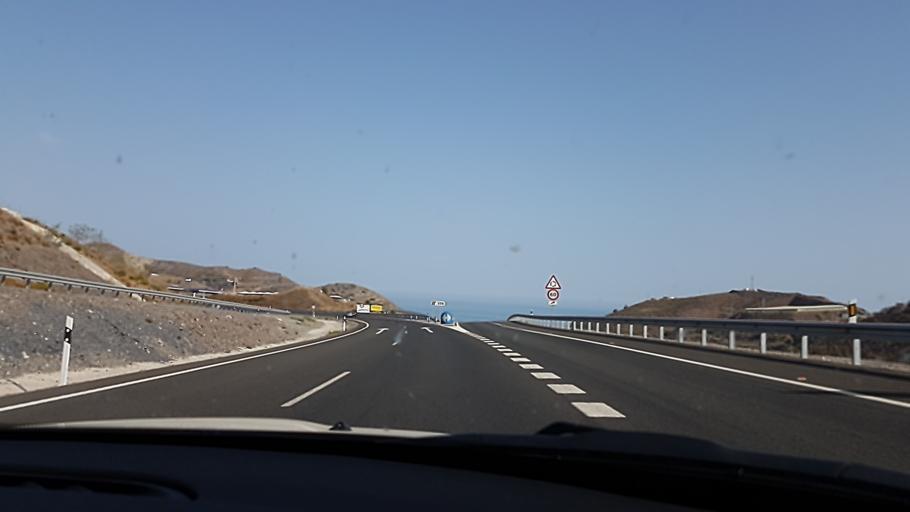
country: ES
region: Andalusia
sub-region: Provincia de Granada
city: Polopos
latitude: 36.7499
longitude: -3.3174
